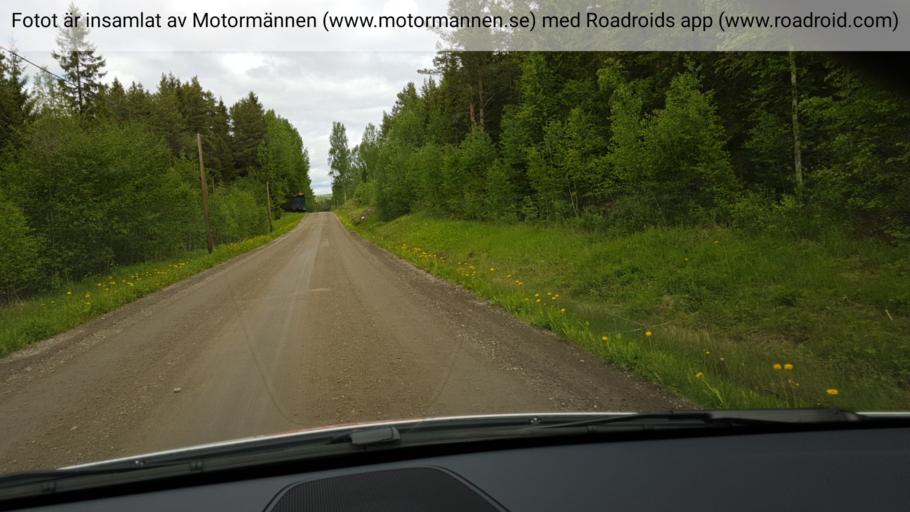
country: SE
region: Jaemtland
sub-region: Braecke Kommun
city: Braecke
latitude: 62.8556
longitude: 15.1807
